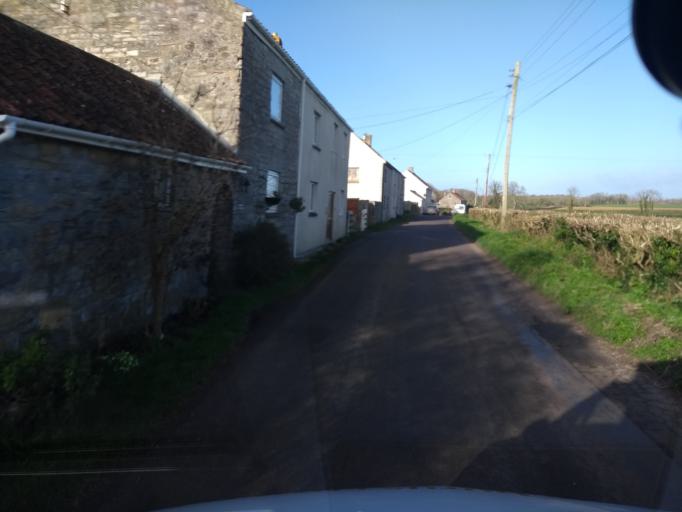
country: GB
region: England
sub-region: Somerset
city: Wedmore
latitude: 51.1356
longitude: -2.8366
